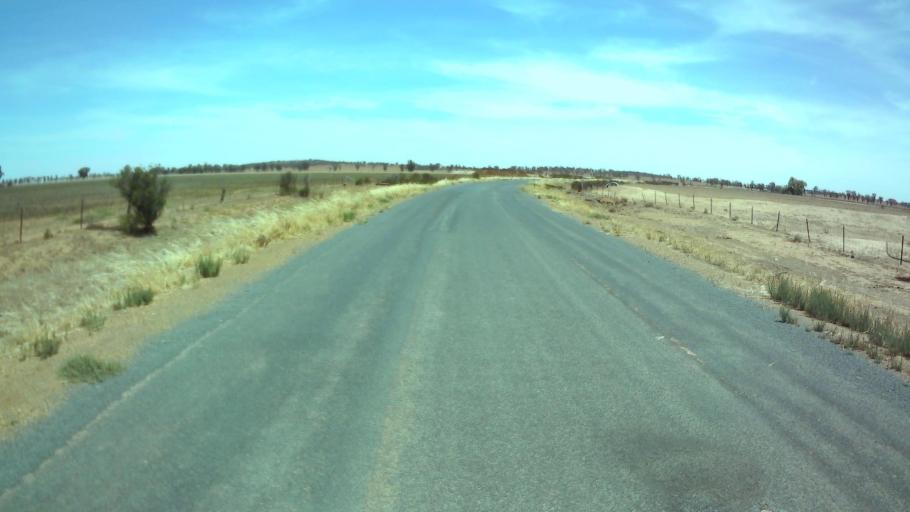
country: AU
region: New South Wales
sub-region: Weddin
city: Grenfell
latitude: -33.7507
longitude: 147.7668
